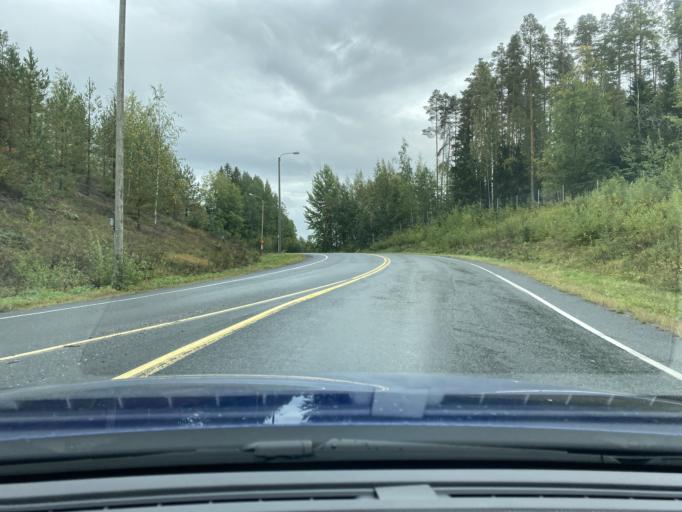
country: FI
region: Pirkanmaa
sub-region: Etelae-Pirkanmaa
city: Kylmaekoski
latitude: 61.1838
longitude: 23.7136
